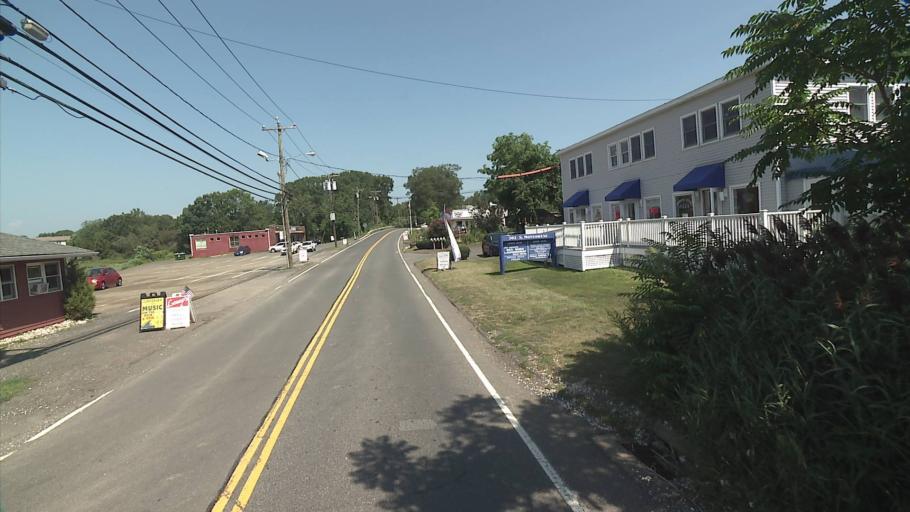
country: US
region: Connecticut
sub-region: New Haven County
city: Branford Center
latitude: 41.2614
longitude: -72.8009
